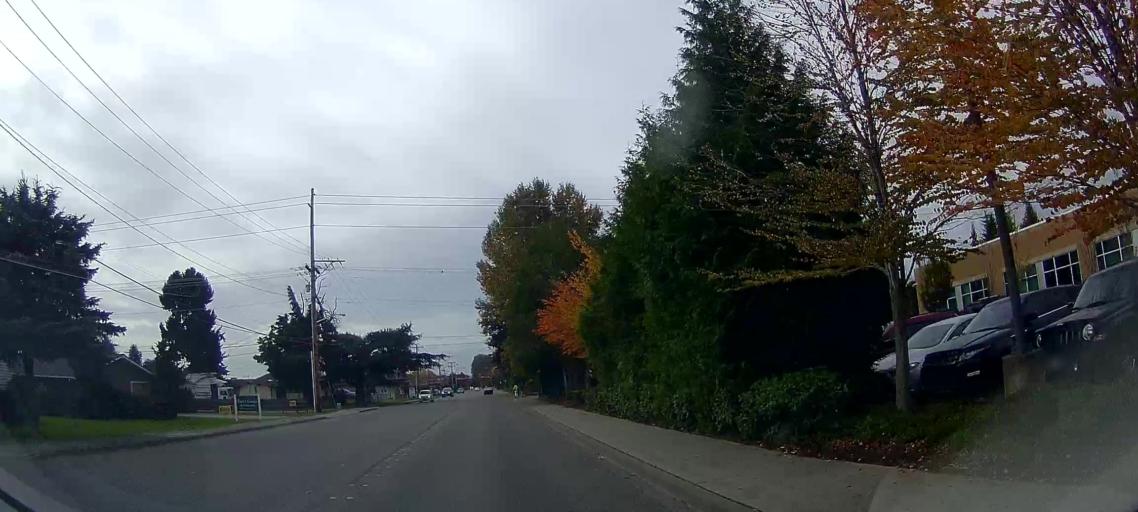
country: US
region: Washington
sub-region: Skagit County
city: Burlington
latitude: 48.4647
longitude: -122.3319
